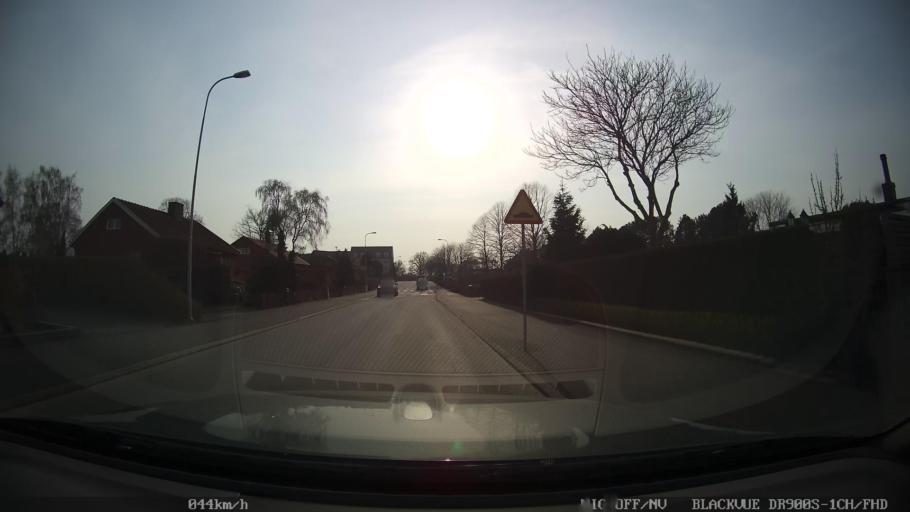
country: SE
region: Skane
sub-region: Ystads Kommun
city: Ystad
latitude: 55.4329
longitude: 13.8059
